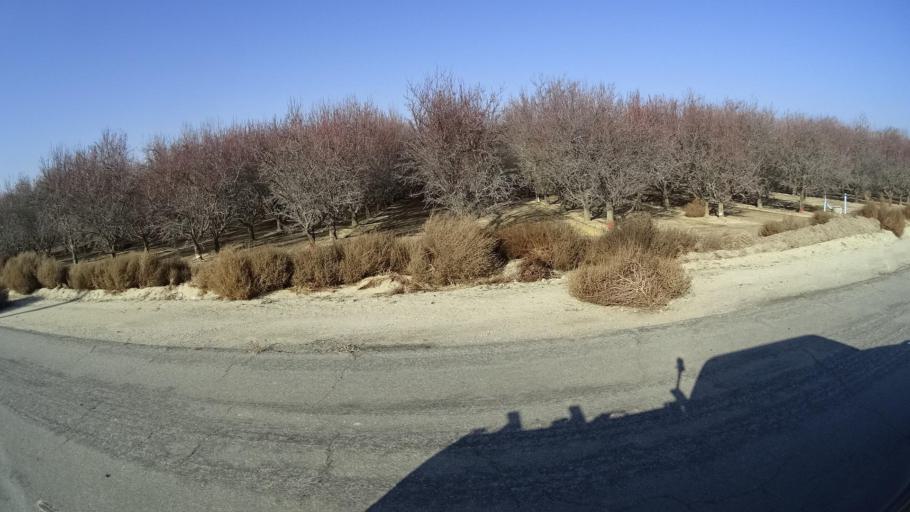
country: US
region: California
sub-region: Kern County
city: Maricopa
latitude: 35.1013
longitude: -119.3564
